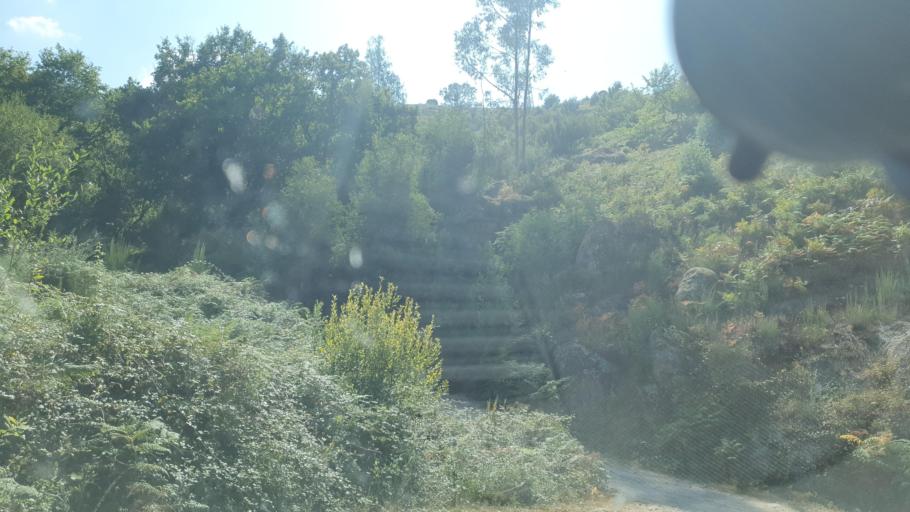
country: PT
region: Braga
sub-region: Vieira do Minho
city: Vieira do Minho
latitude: 41.6717
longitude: -8.1337
